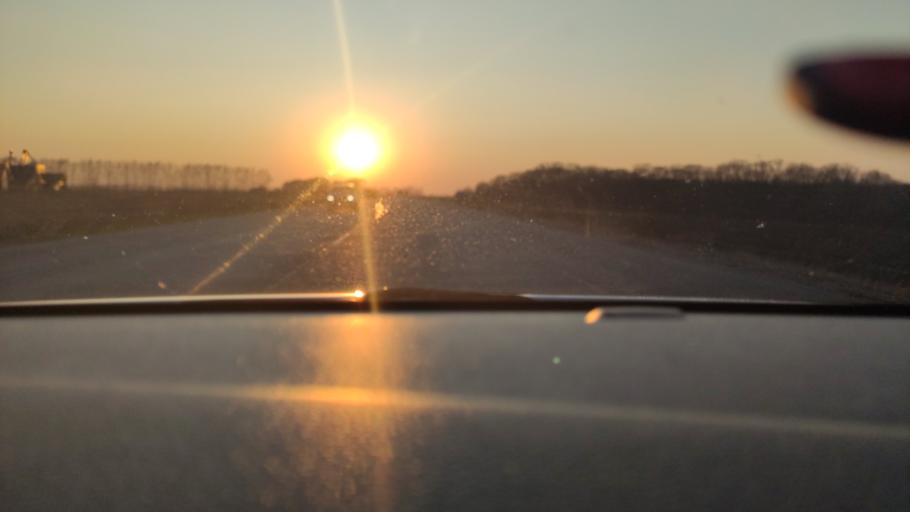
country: RU
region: Voronezj
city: Kolodeznyy
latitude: 51.3401
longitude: 39.0426
